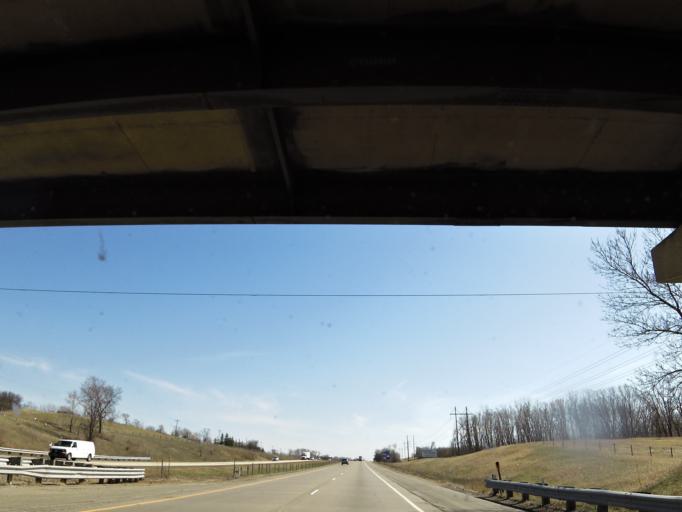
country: US
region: Minnesota
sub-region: Dakota County
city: Lakeville
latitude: 44.6670
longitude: -93.2943
